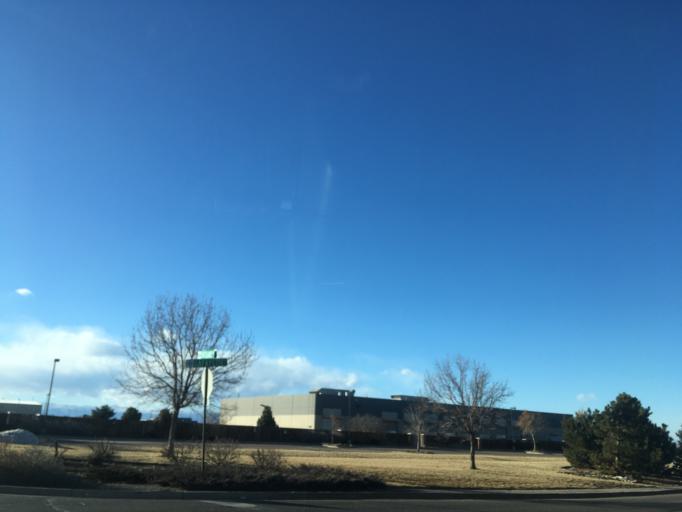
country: US
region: Colorado
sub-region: Adams County
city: Northglenn
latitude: 39.9227
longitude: -104.9688
